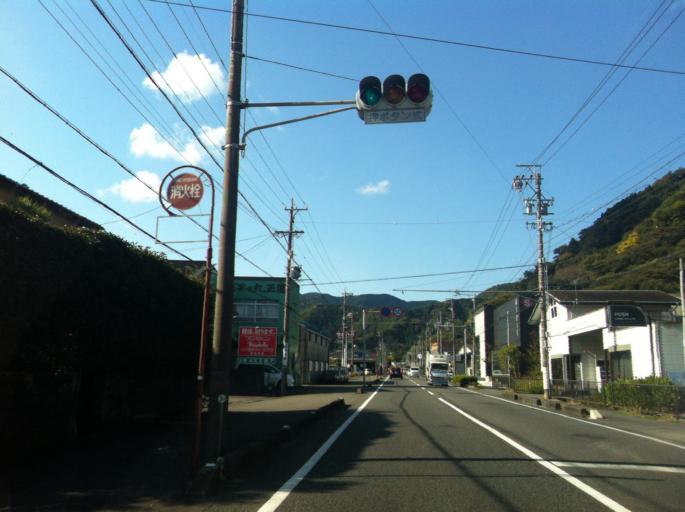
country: JP
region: Shizuoka
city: Shizuoka-shi
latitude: 34.9500
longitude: 138.3427
